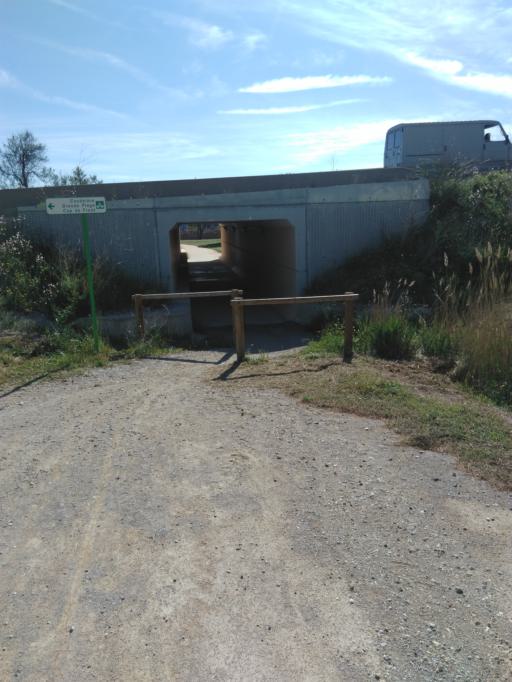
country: FR
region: Languedoc-Roussillon
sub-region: Departement des Pyrenees-Orientales
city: Le Barcares
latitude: 42.8078
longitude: 3.0309
